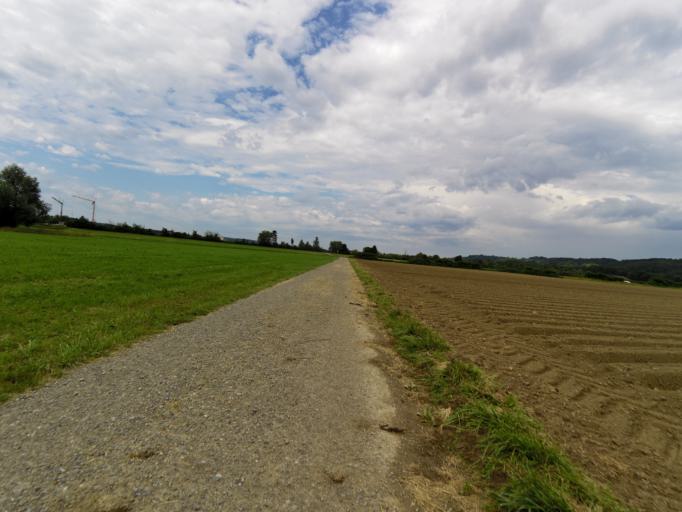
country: CH
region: Thurgau
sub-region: Frauenfeld District
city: Frauenfeld
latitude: 47.5696
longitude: 8.8726
